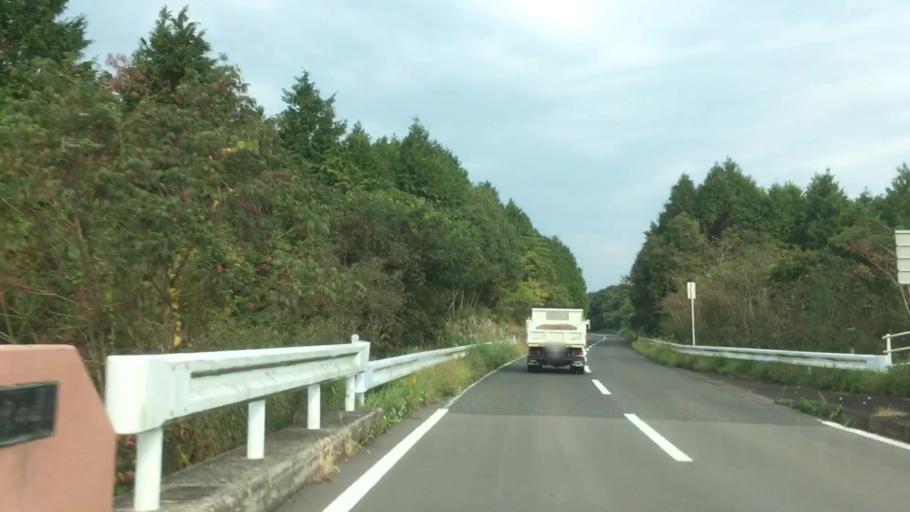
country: JP
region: Nagasaki
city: Sasebo
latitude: 33.0290
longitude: 129.6903
